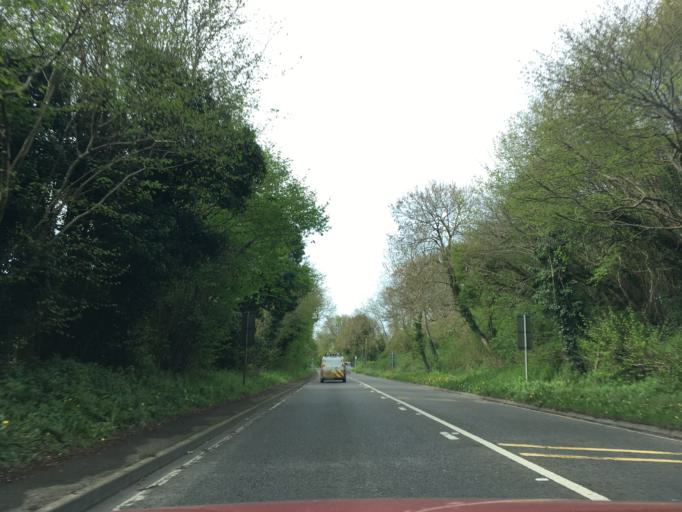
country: GB
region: England
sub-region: Bath and North East Somerset
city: Peasedown Saint John
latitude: 51.3297
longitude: -2.4098
